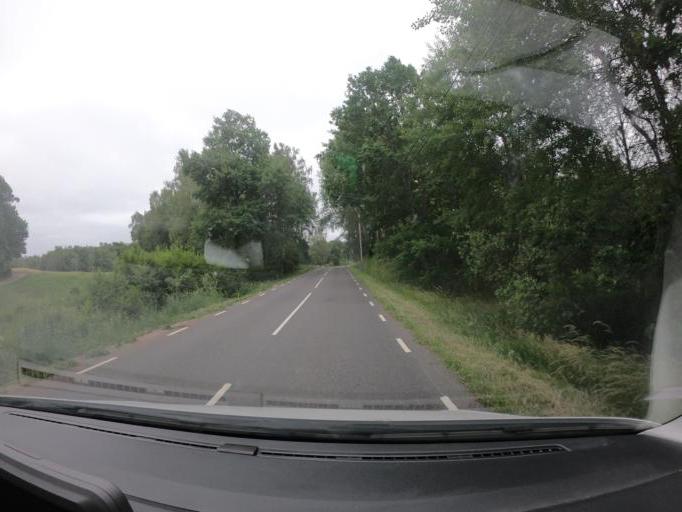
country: SE
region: Skane
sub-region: Perstorps Kommun
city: Perstorp
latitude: 56.0386
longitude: 13.3646
